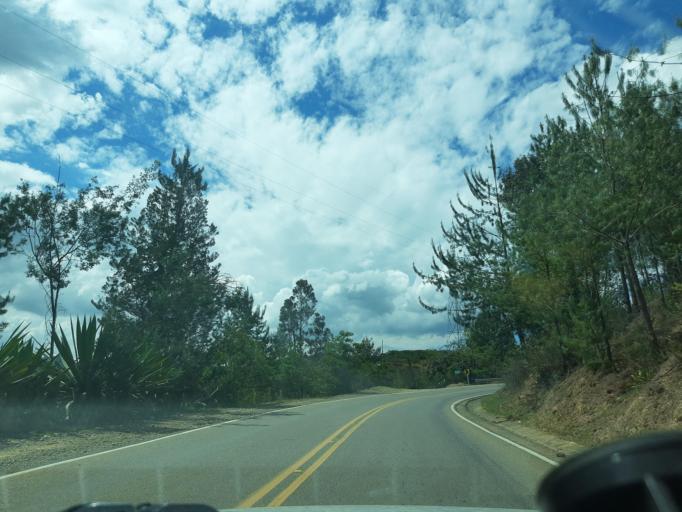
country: CO
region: Boyaca
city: Raquira
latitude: 5.5669
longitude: -73.6607
